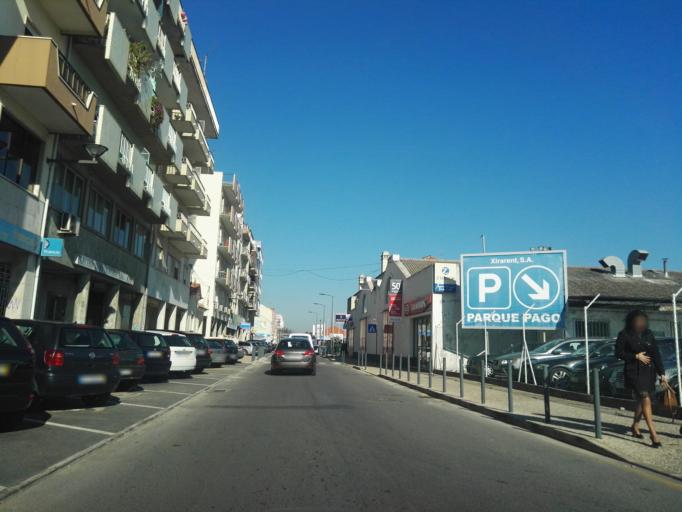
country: PT
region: Lisbon
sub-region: Vila Franca de Xira
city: Vila Franca de Xira
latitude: 38.9573
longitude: -8.9861
